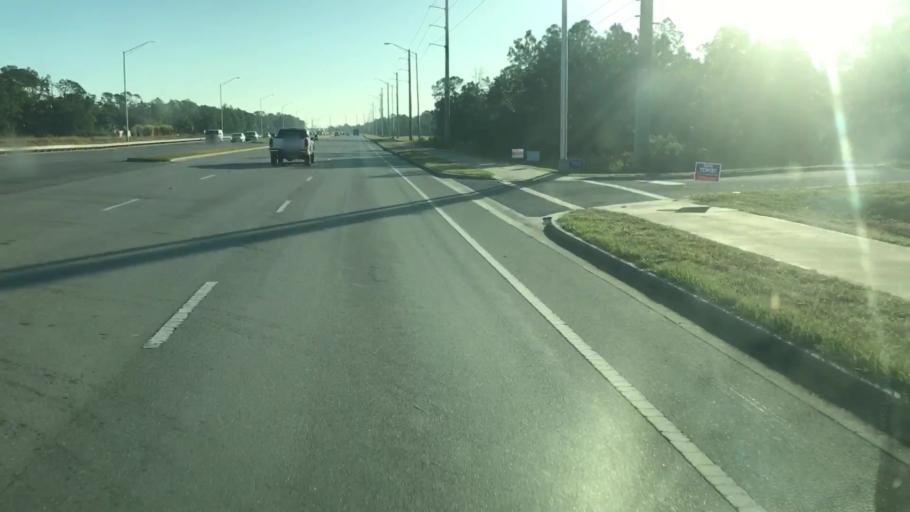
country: US
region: Florida
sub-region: Collier County
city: Orangetree
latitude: 26.2759
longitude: -81.6149
